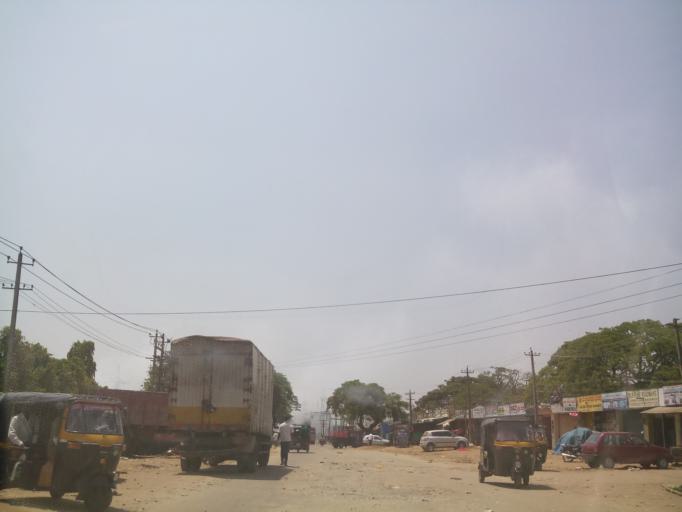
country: IN
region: Karnataka
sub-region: Hassan
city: Hassan
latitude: 12.9999
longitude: 76.0940
